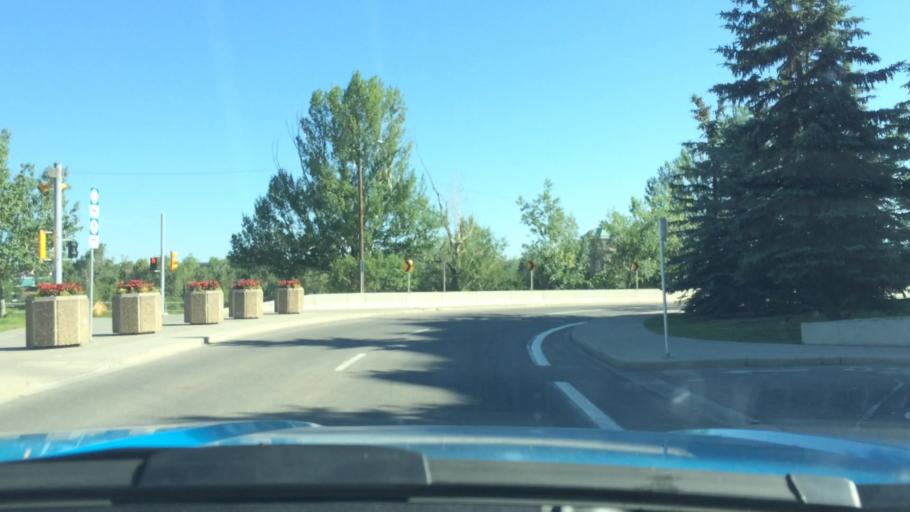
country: CA
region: Alberta
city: Calgary
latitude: 51.0484
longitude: -114.0884
